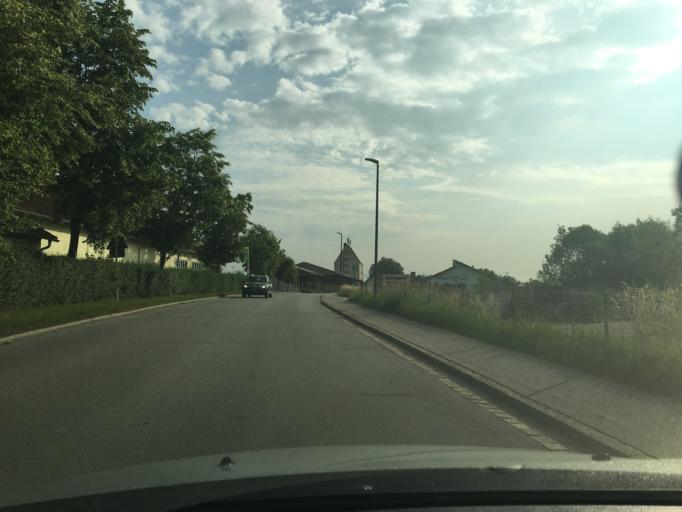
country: DE
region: Bavaria
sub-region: Upper Bavaria
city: Neumarkt-Sankt Veit
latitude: 48.3568
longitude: 12.4972
